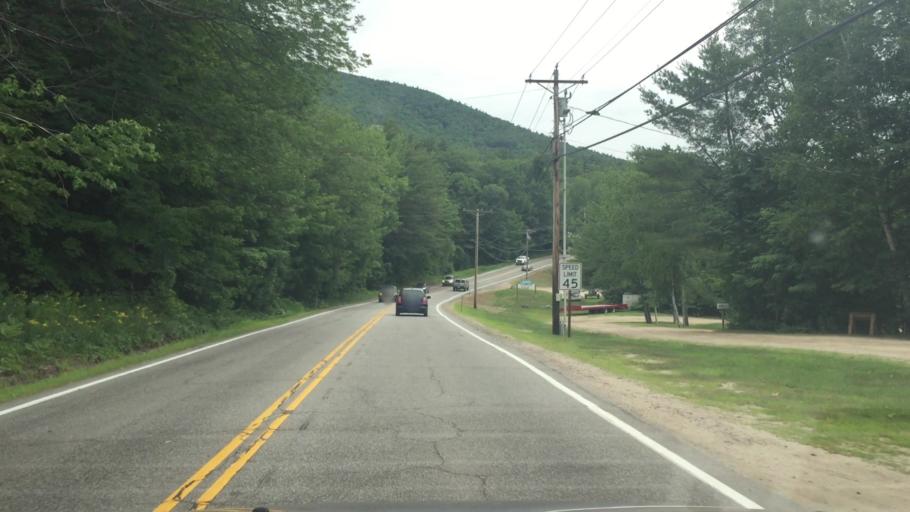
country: US
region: New Hampshire
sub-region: Carroll County
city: Center Harbor
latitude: 43.7248
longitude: -71.4309
